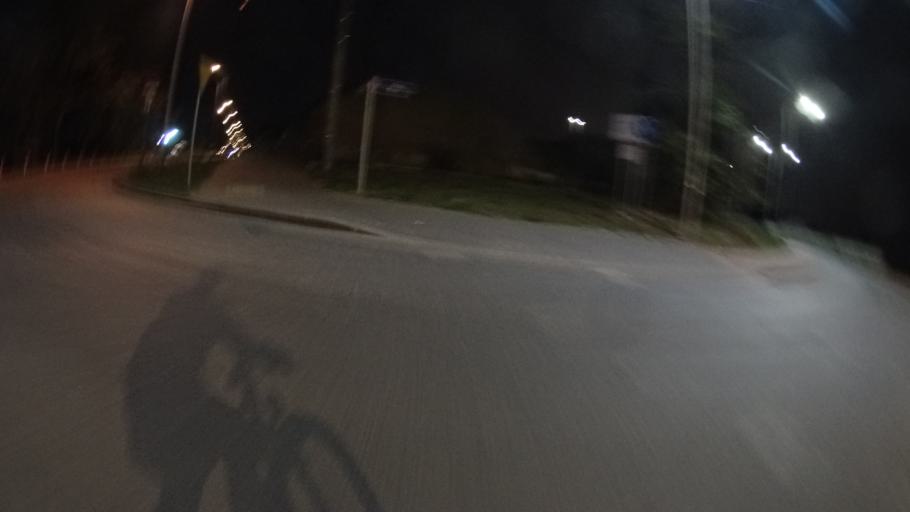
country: PL
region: Masovian Voivodeship
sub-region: Powiat pruszkowski
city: Otrebusy
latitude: 52.1579
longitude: 20.7652
